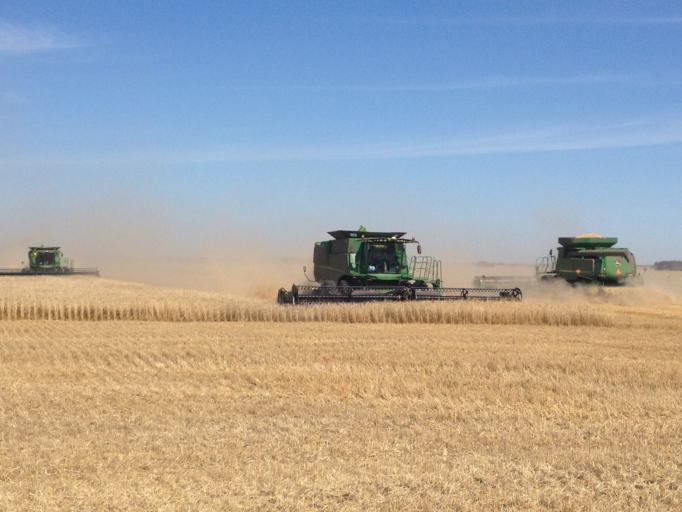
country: US
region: North Dakota
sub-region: Mercer County
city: Beulah
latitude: 47.6958
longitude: -101.8925
